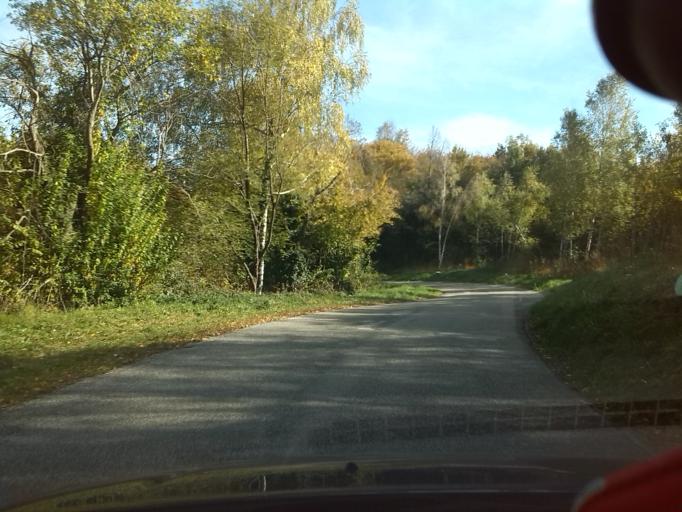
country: IT
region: Friuli Venezia Giulia
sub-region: Provincia di Udine
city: San Leonardo
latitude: 46.0991
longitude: 13.5470
